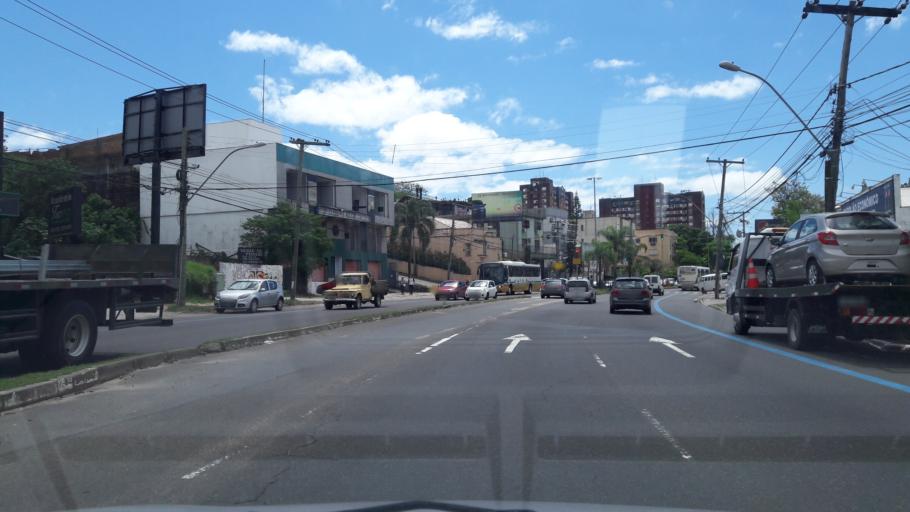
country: BR
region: Rio Grande do Sul
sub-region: Porto Alegre
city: Porto Alegre
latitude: -30.1062
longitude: -51.2291
